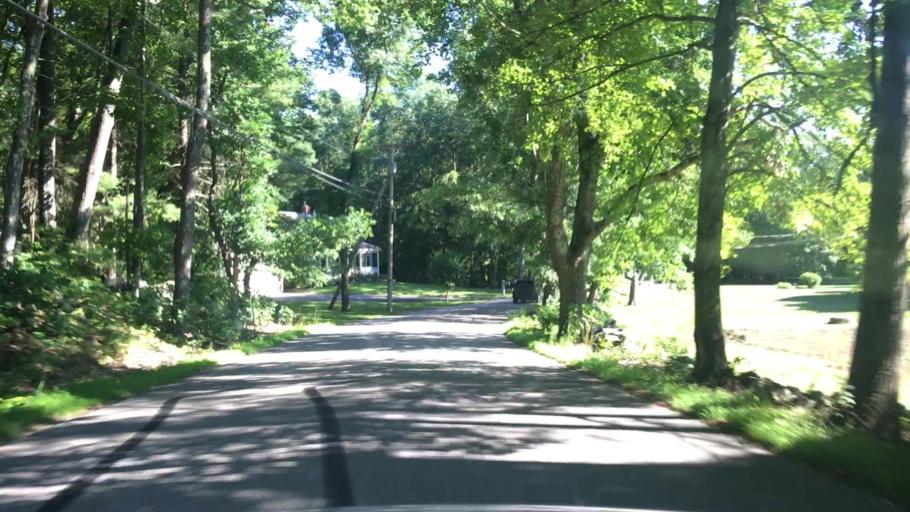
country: US
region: New Hampshire
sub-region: Rockingham County
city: Exeter
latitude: 43.0262
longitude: -70.9720
